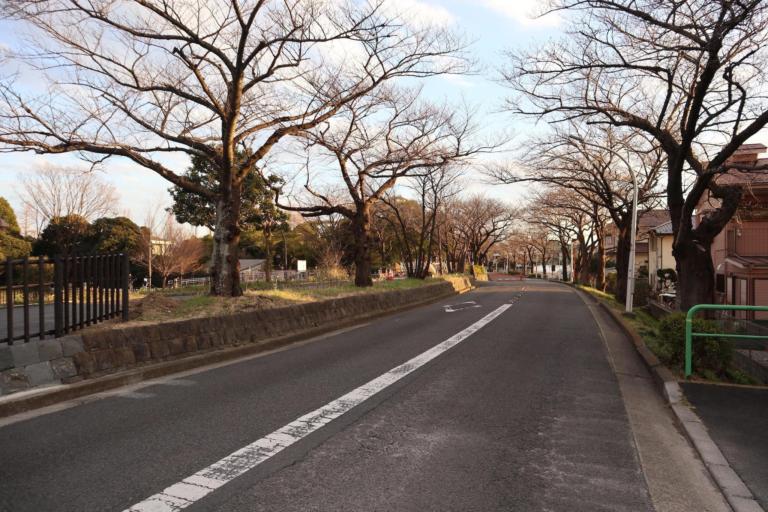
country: JP
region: Chiba
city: Matsudo
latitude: 35.7870
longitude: 139.8684
